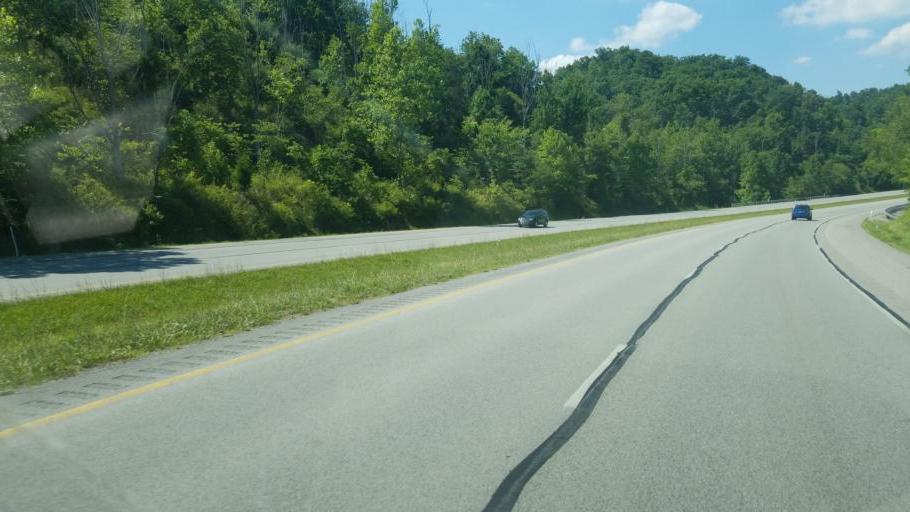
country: US
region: West Virginia
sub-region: Kanawha County
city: Sissonville
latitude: 38.5759
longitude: -81.6412
